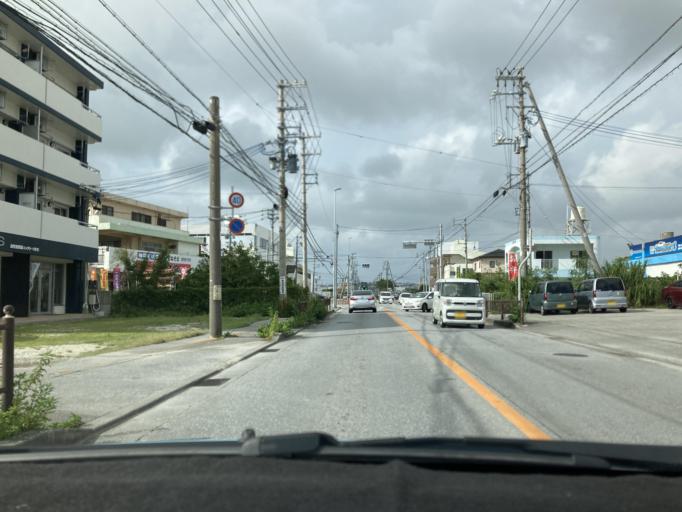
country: JP
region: Okinawa
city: Tomigusuku
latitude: 26.1641
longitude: 127.6688
